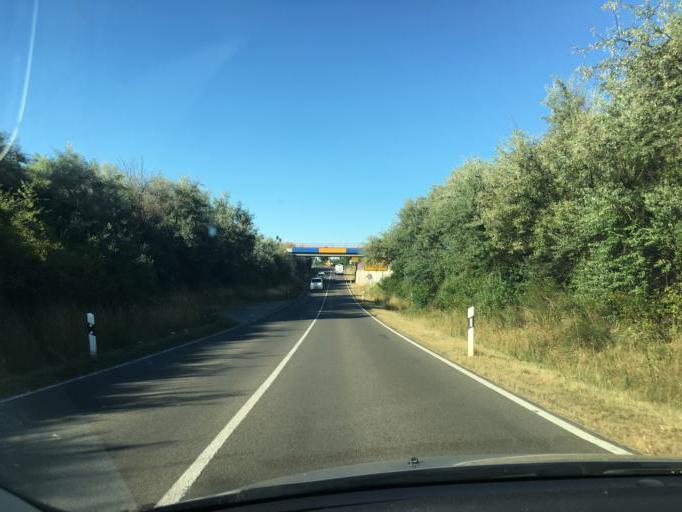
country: DE
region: Saxony
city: Grossposna
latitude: 51.2668
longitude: 12.4857
